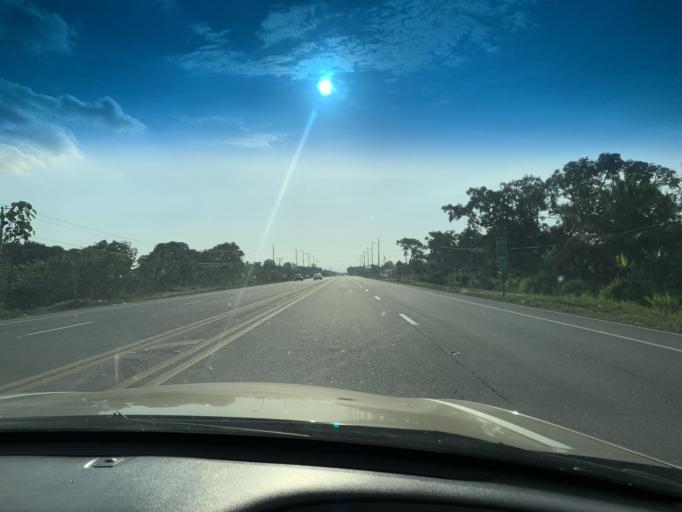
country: EC
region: Guayas
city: Naranjito
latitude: -2.2568
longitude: -79.5849
